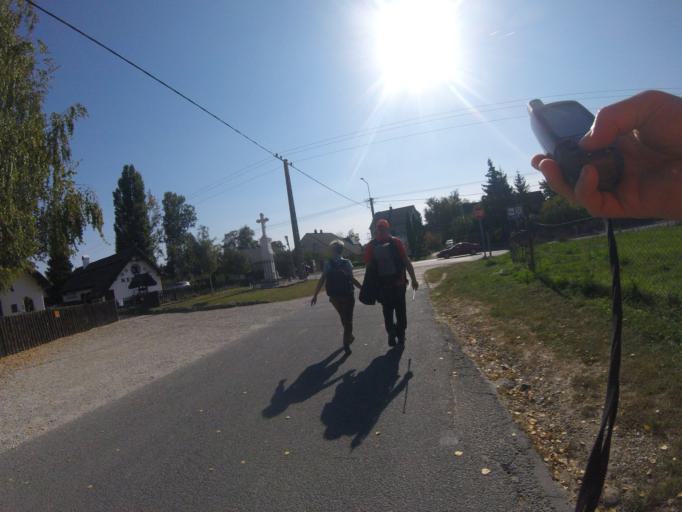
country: HU
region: Zala
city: Gyenesdias
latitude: 46.7740
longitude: 17.2794
